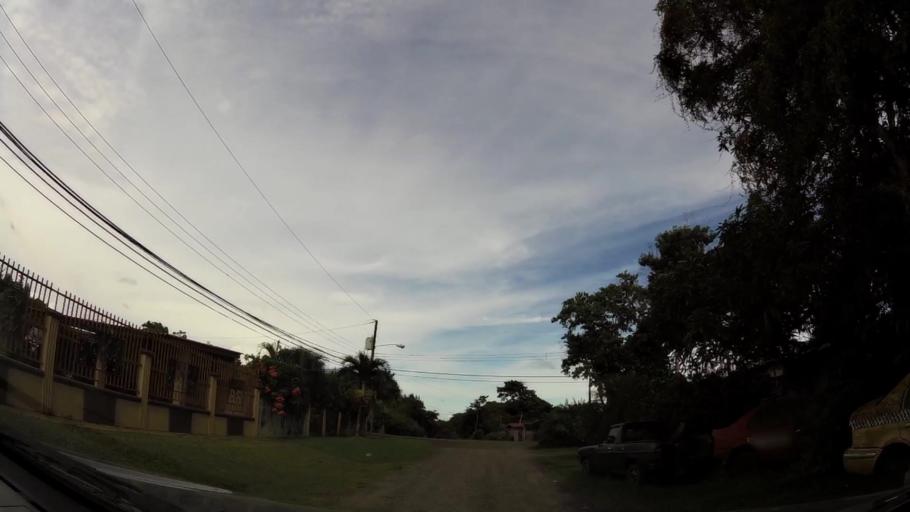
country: PA
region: Panama
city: El Coco
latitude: 8.8659
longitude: -79.8056
